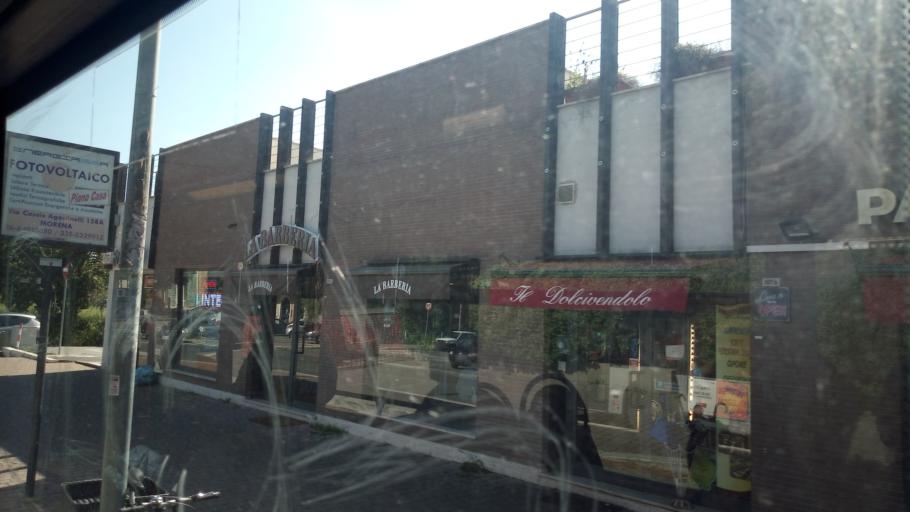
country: IT
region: Latium
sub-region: Citta metropolitana di Roma Capitale
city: Ciampino
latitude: 41.8129
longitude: 12.6043
